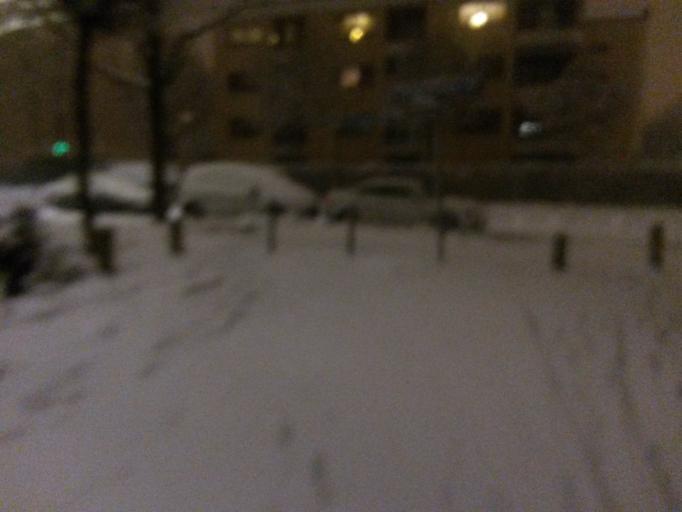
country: DE
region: Bavaria
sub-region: Upper Bavaria
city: Neubiberg
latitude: 48.0928
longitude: 11.6438
